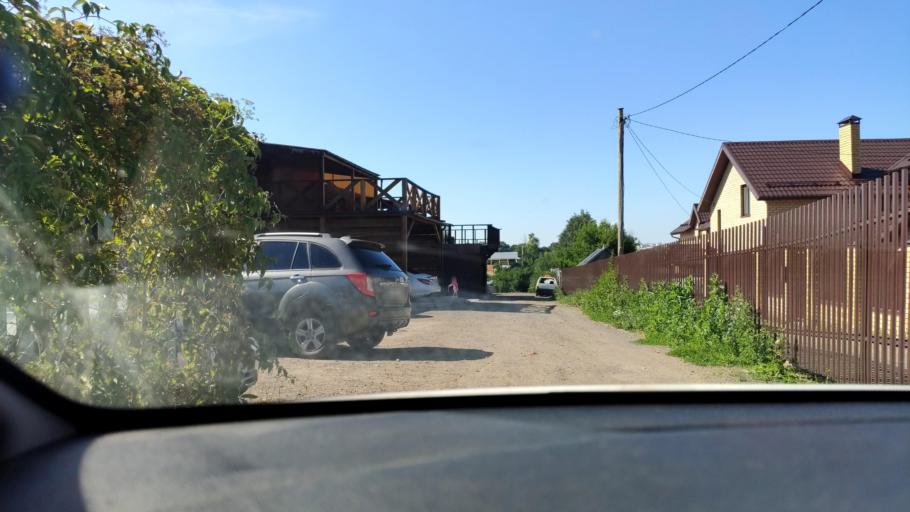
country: RU
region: Tatarstan
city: Vysokaya Gora
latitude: 55.8002
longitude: 49.2677
